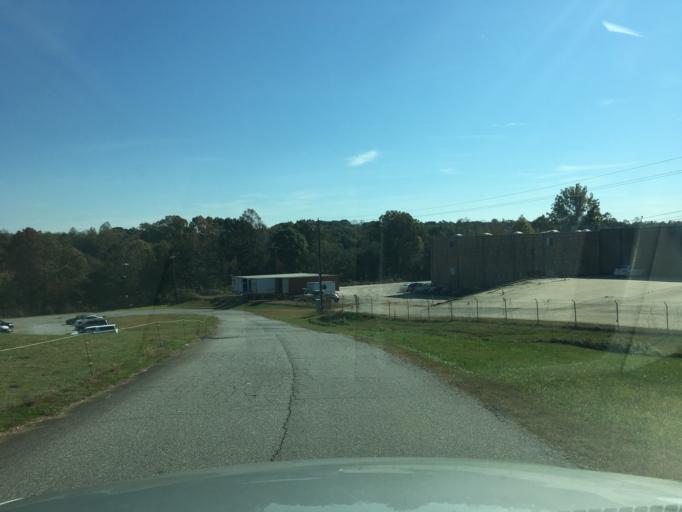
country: US
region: North Carolina
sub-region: Catawba County
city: Conover
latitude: 35.7117
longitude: -81.2461
